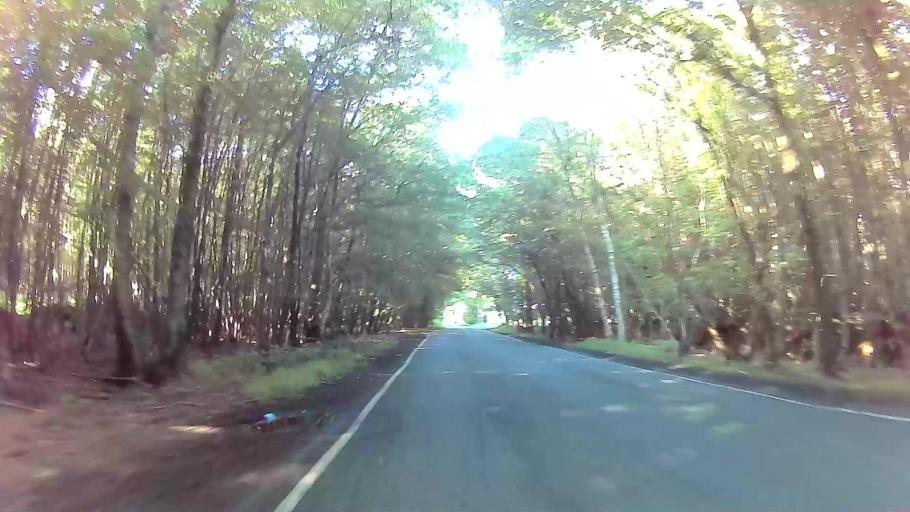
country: GB
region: England
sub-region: Essex
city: Ingatestone
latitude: 51.6999
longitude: 0.3517
